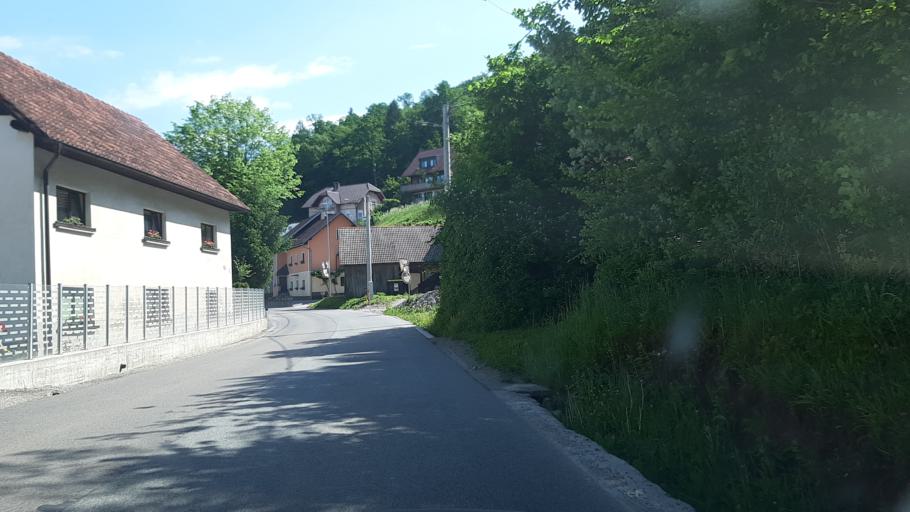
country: SI
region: Brezovica
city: Notranje Gorice
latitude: 45.9686
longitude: 14.4153
